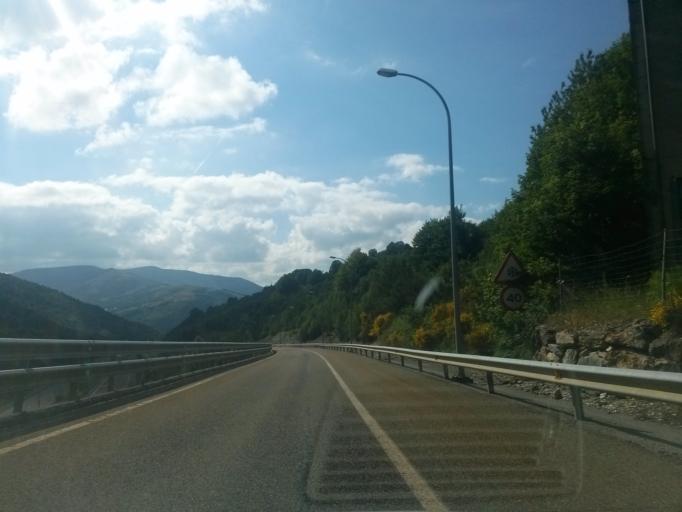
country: ES
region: Castille and Leon
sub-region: Provincia de Leon
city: Balboa
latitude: 42.7257
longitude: -7.0271
